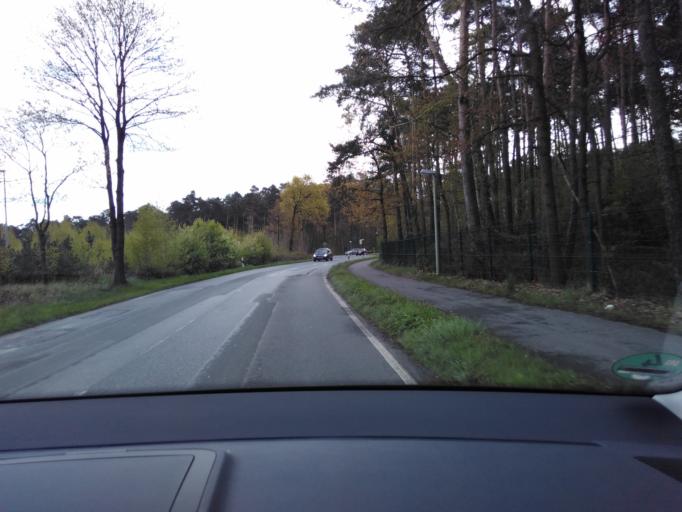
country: DE
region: North Rhine-Westphalia
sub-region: Regierungsbezirk Detmold
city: Verl
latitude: 51.8852
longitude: 8.4576
